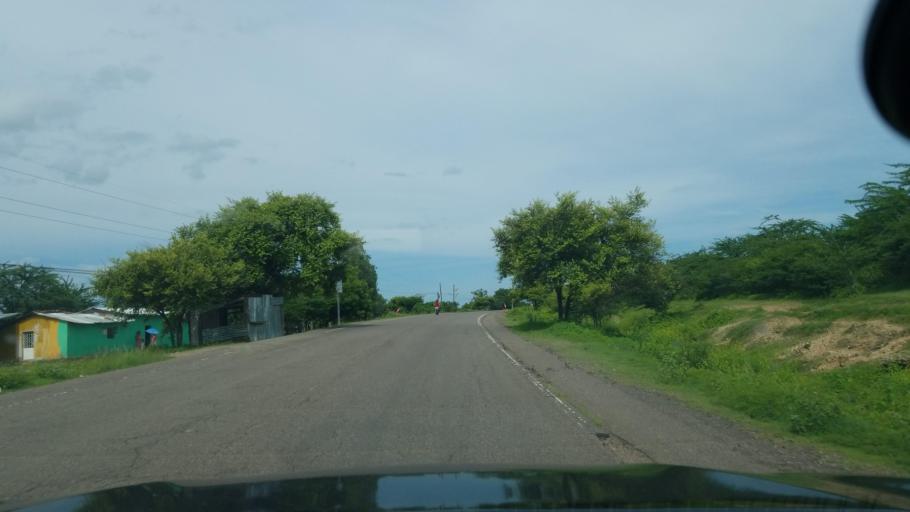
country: HN
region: Choluteca
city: Santa Ana de Yusguare
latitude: 13.3508
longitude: -87.1082
